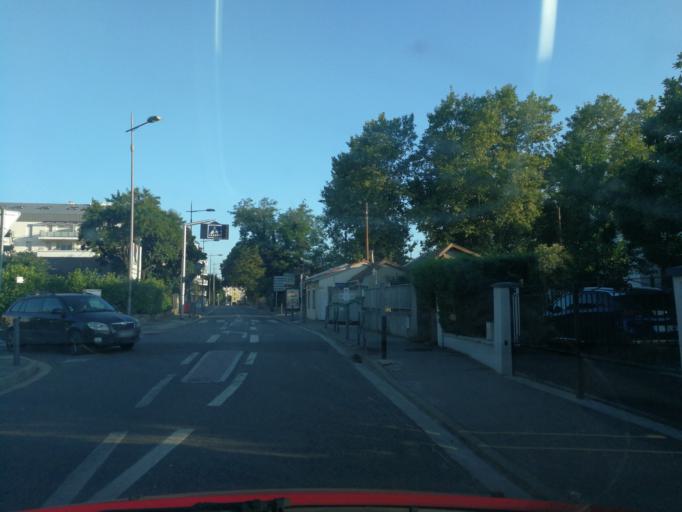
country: FR
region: Midi-Pyrenees
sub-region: Departement de la Haute-Garonne
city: Balma
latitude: 43.6100
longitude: 1.4794
